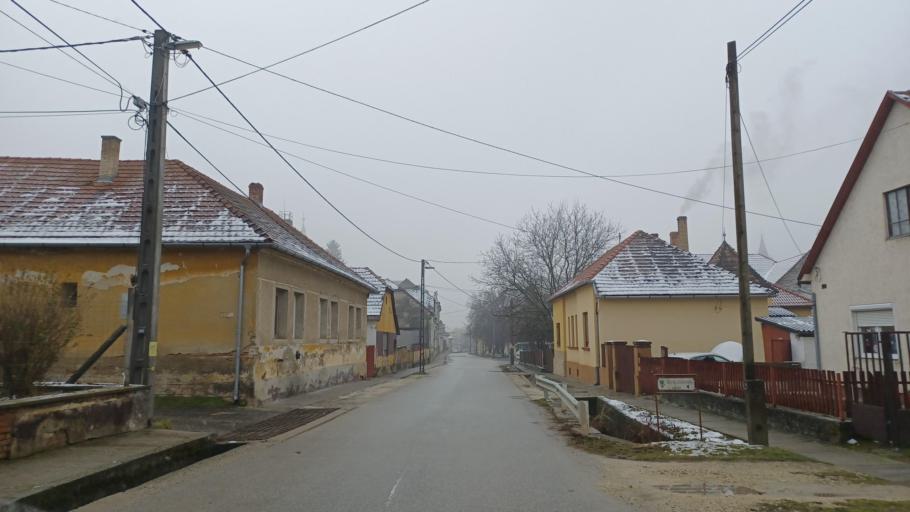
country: HU
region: Tolna
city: Gyonk
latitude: 46.5585
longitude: 18.4783
